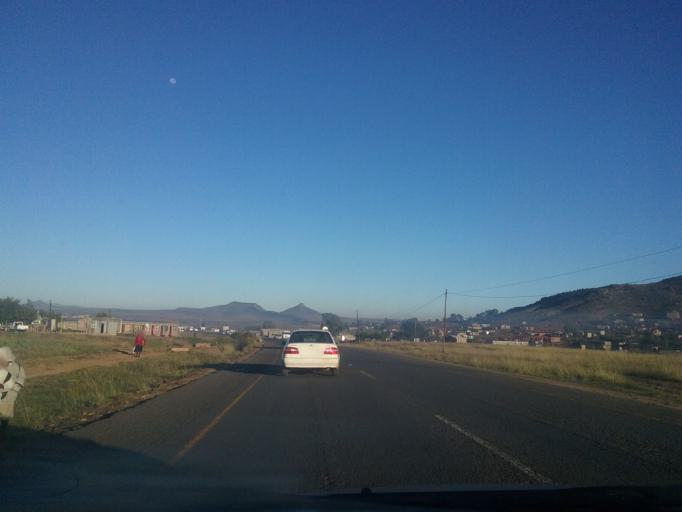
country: LS
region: Mohale's Hoek District
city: Mohale's Hoek
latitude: -30.1492
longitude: 27.4507
